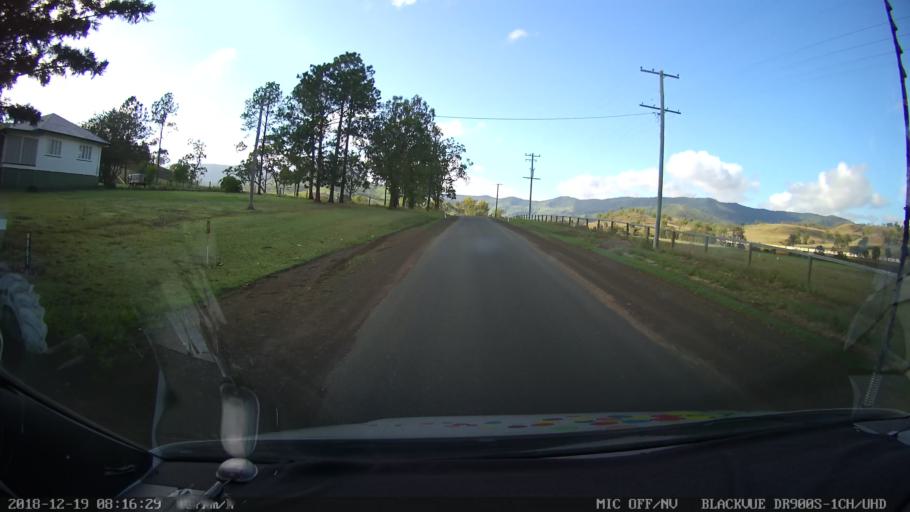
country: AU
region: New South Wales
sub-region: Kyogle
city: Kyogle
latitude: -28.2583
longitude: 152.9065
